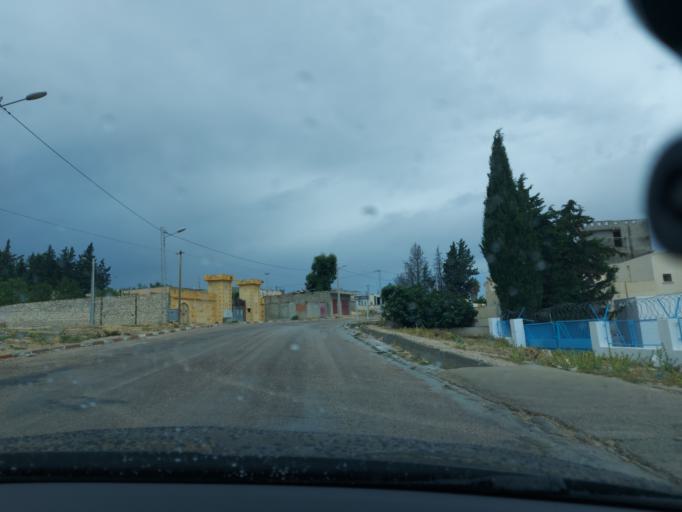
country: TN
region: Silyanah
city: Maktar
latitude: 35.8536
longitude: 9.2126
